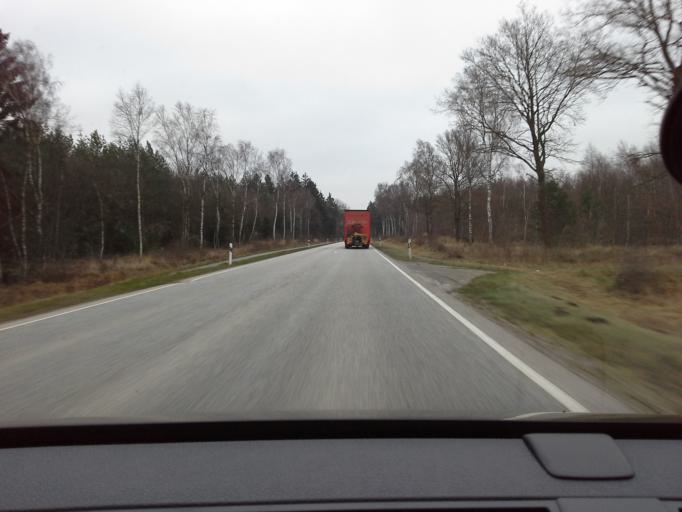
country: DE
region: Schleswig-Holstein
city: Lentfohrden
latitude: 53.8403
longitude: 9.8857
